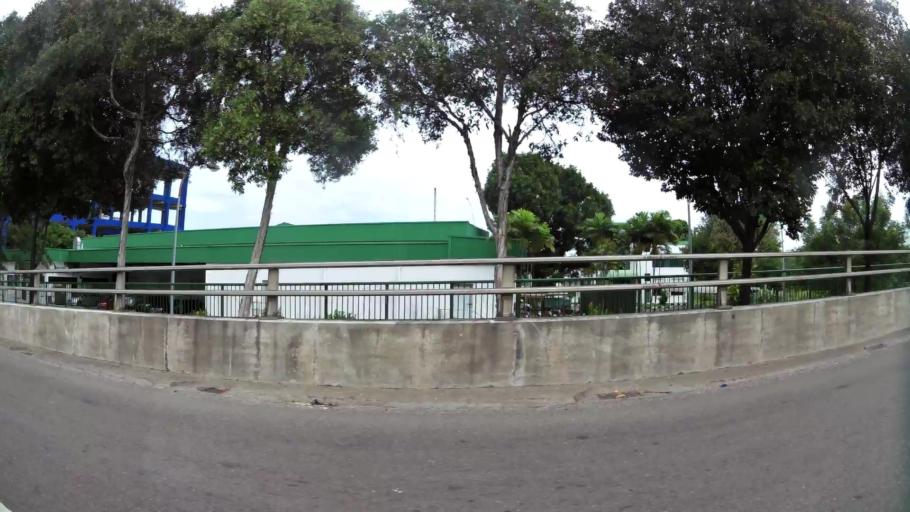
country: SG
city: Singapore
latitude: 1.3132
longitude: 103.7254
